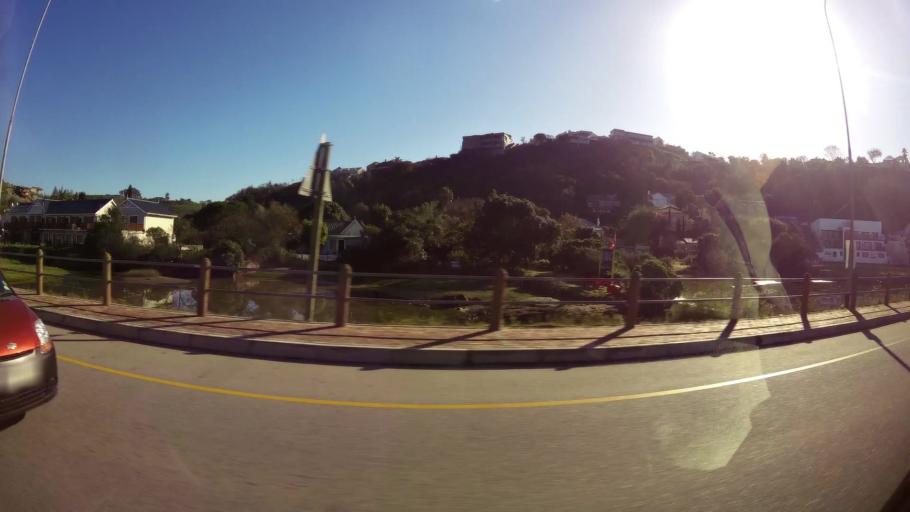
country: ZA
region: Western Cape
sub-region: Eden District Municipality
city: Knysna
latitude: -34.0370
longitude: 23.0272
